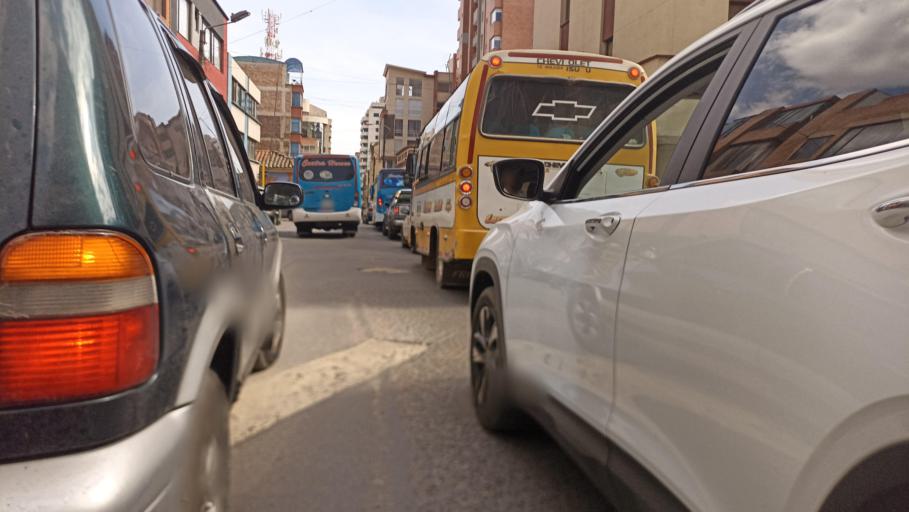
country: CO
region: Boyaca
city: Duitama
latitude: 5.8300
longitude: -73.0355
